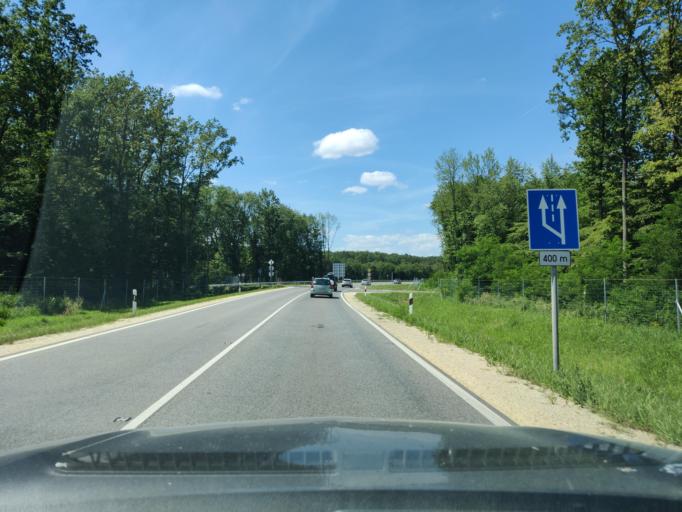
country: HU
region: Vas
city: Kormend
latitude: 47.0288
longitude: 16.6144
